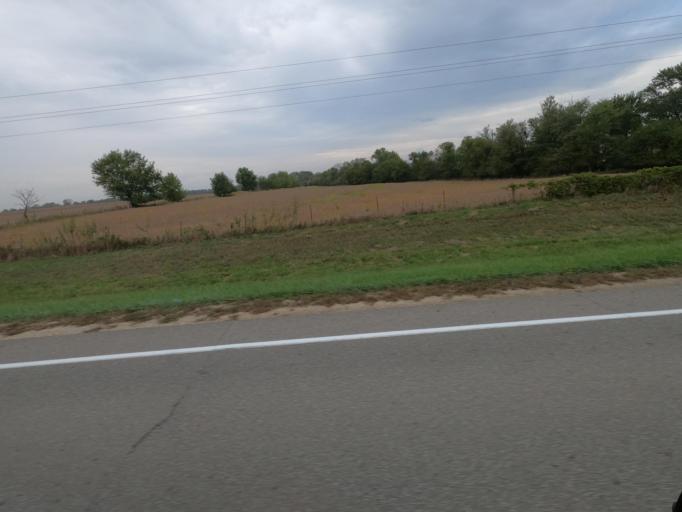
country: US
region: Iowa
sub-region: Henry County
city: Mount Pleasant
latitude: 40.8134
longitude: -91.7230
